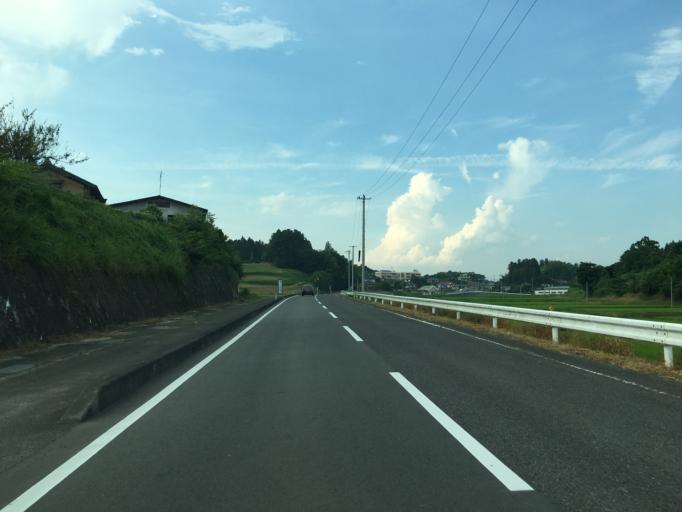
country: JP
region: Fukushima
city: Motomiya
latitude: 37.5203
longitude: 140.4439
